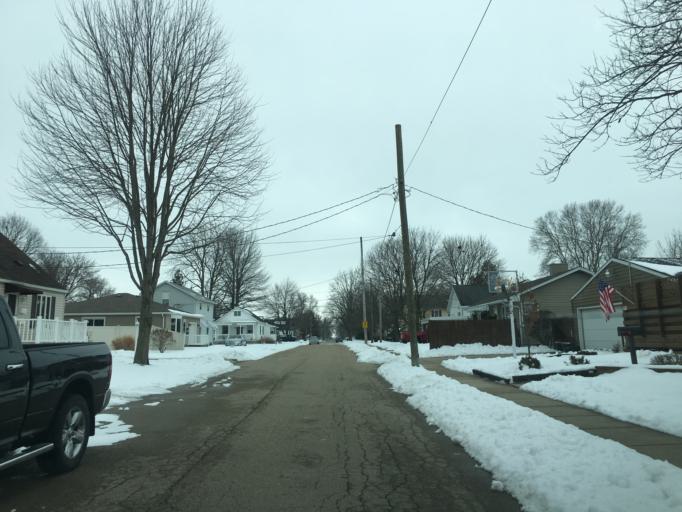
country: US
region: Illinois
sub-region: LaSalle County
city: Peru
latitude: 41.3338
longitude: -89.1332
